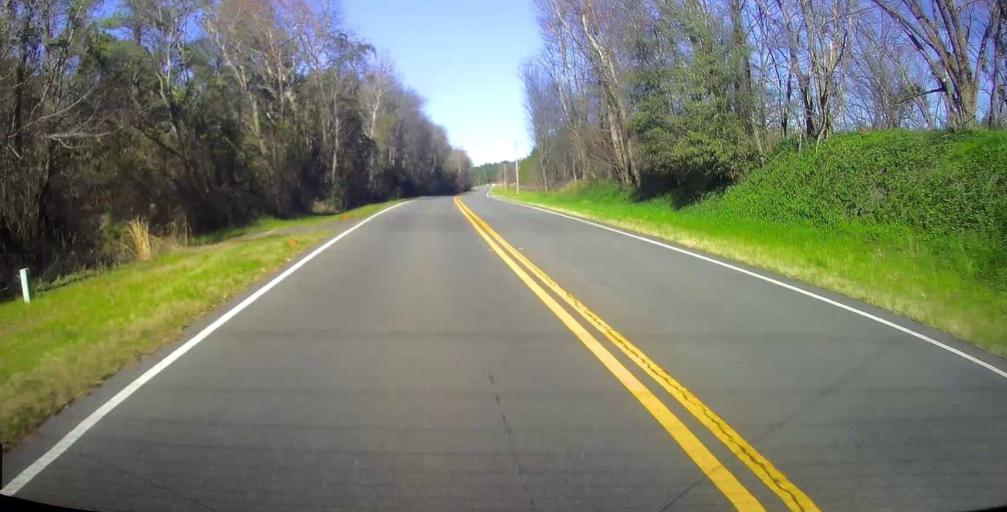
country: US
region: Georgia
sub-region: Macon County
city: Montezuma
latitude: 32.3553
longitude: -84.0170
